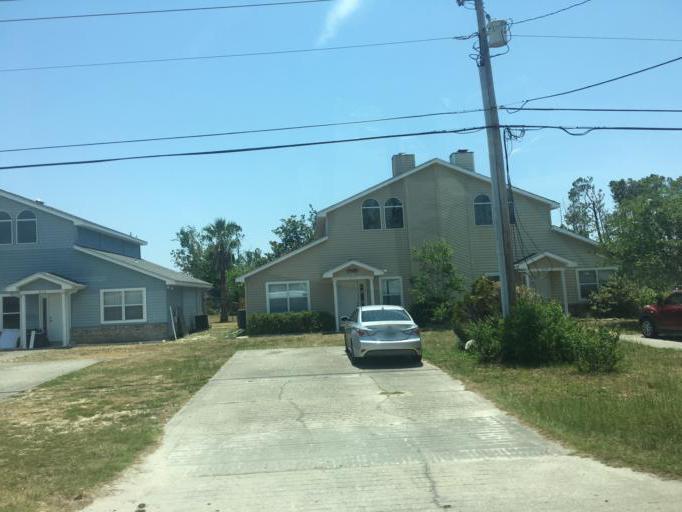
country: US
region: Florida
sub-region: Bay County
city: Lynn Haven
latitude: 30.2187
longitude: -85.6568
